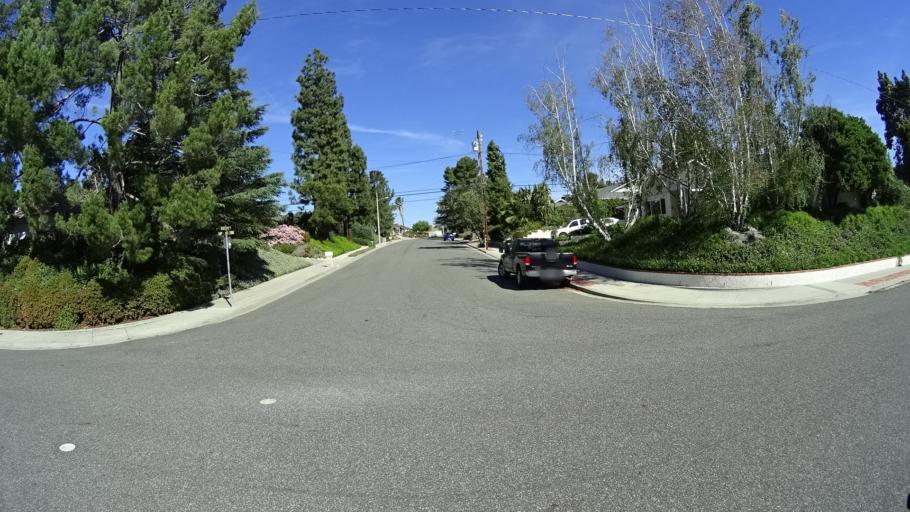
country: US
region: California
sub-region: Ventura County
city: Thousand Oaks
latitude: 34.2225
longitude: -118.8618
